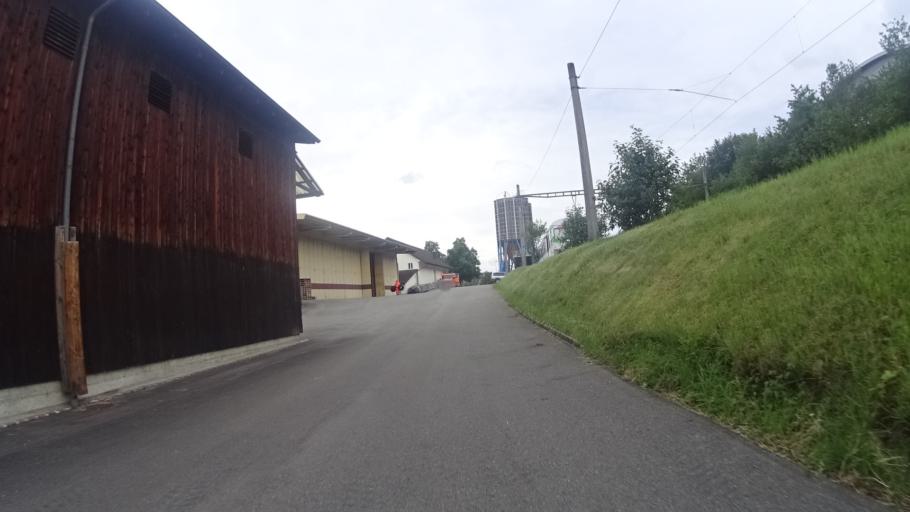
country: DE
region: Baden-Wuerttemberg
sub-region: Freiburg Region
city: Waldshut-Tiengen
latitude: 47.6073
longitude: 8.2208
